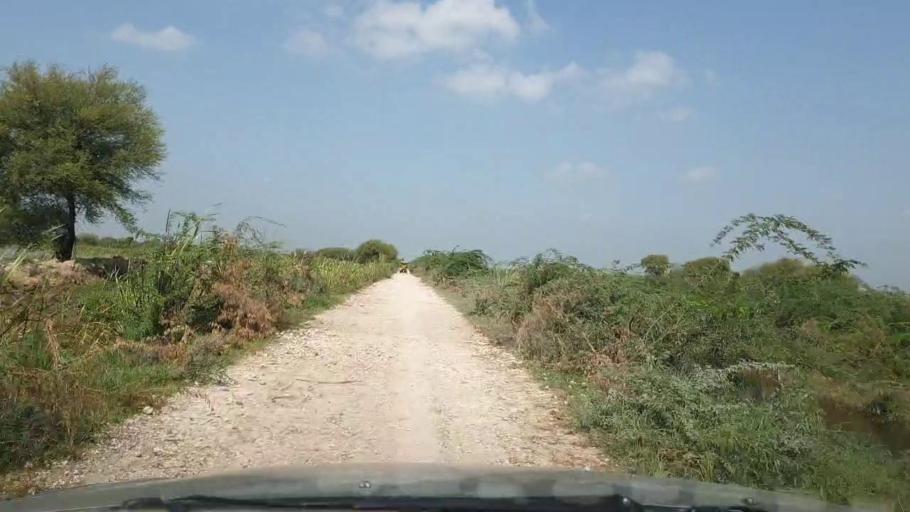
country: PK
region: Sindh
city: Rajo Khanani
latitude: 25.0194
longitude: 68.9165
